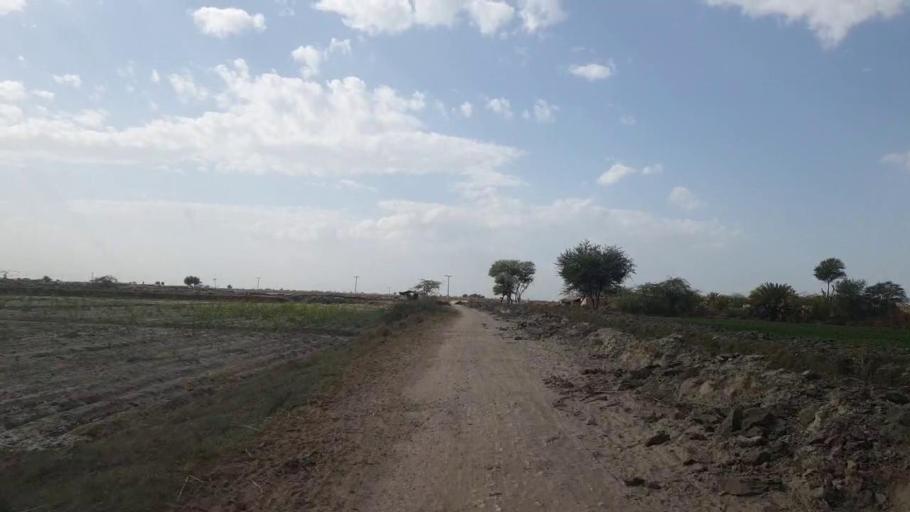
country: PK
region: Sindh
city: Shahdadpur
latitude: 25.9892
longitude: 68.4682
